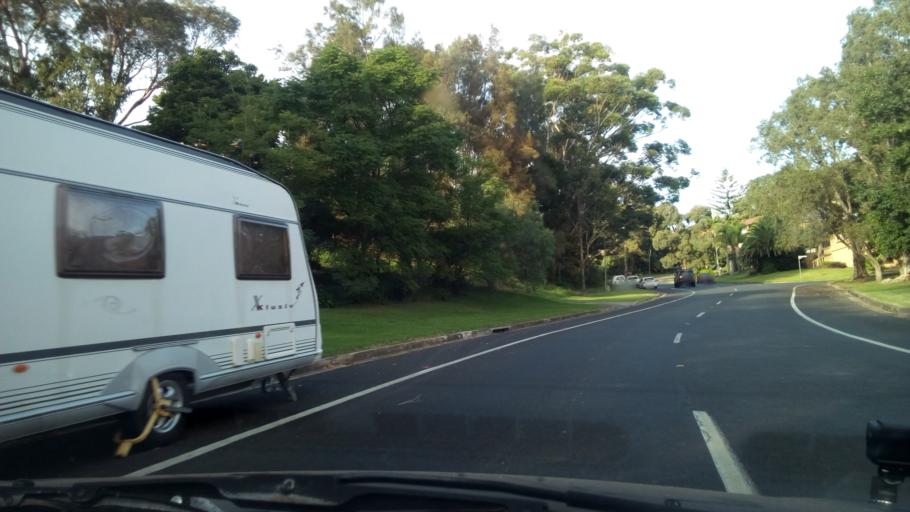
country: AU
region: New South Wales
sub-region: Wollongong
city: Mount Ousley
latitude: -34.3911
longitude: 150.8744
